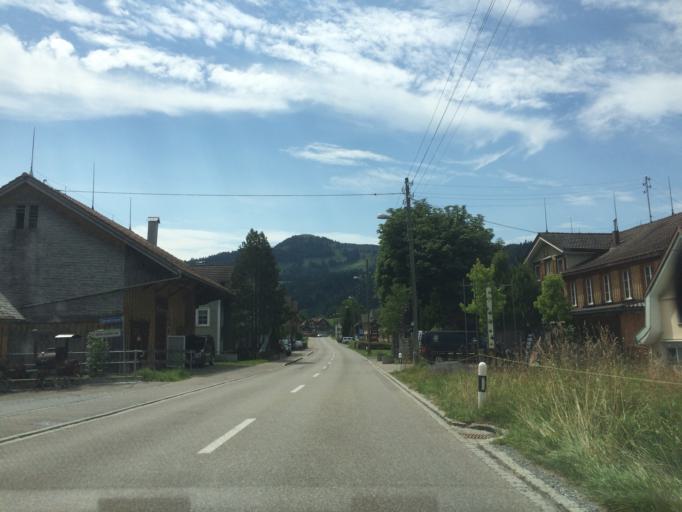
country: CH
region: Appenzell Ausserrhoden
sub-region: Bezirk Hinterland
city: Urnasch
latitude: 47.3074
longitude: 9.2761
